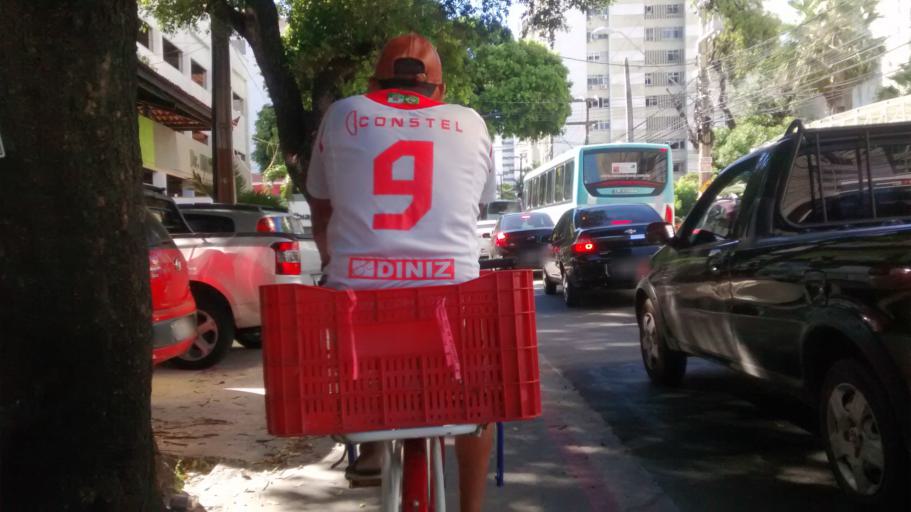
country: BR
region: Ceara
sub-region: Fortaleza
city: Fortaleza
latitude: -3.7341
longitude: -38.5049
